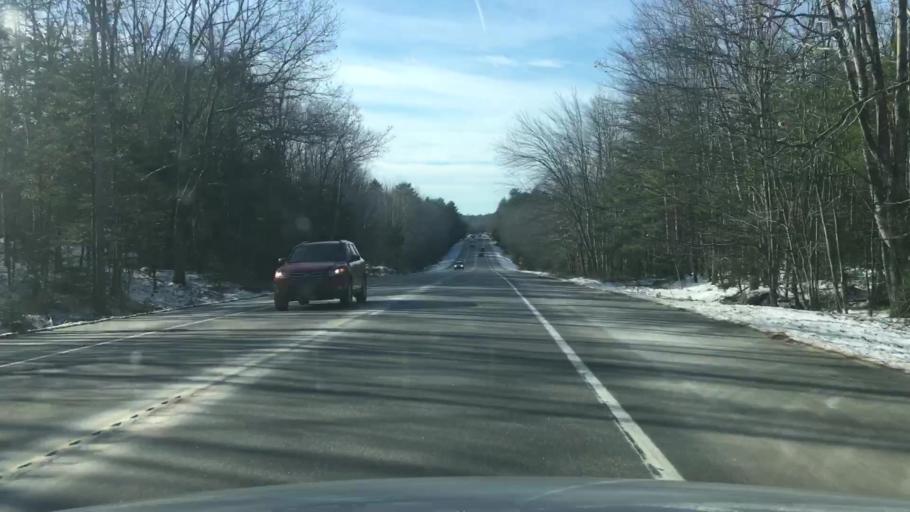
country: US
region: Maine
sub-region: Sagadahoc County
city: Woolwich
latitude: 43.9538
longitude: -69.7401
